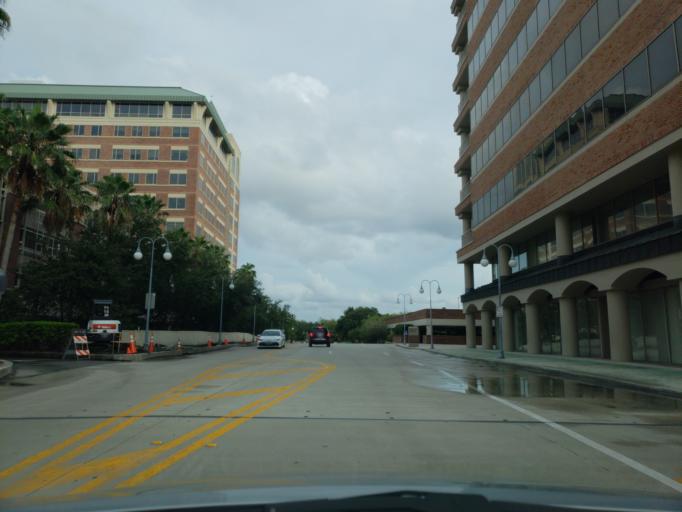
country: US
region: Florida
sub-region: Hillsborough County
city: Tampa
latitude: 27.9383
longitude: -82.4538
